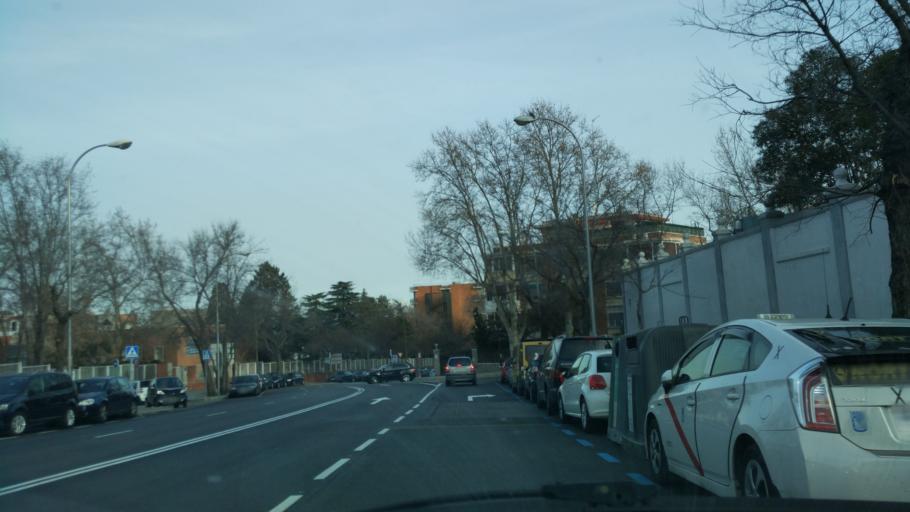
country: ES
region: Madrid
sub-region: Provincia de Madrid
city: Moncloa-Aravaca
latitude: 40.4431
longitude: -3.7192
